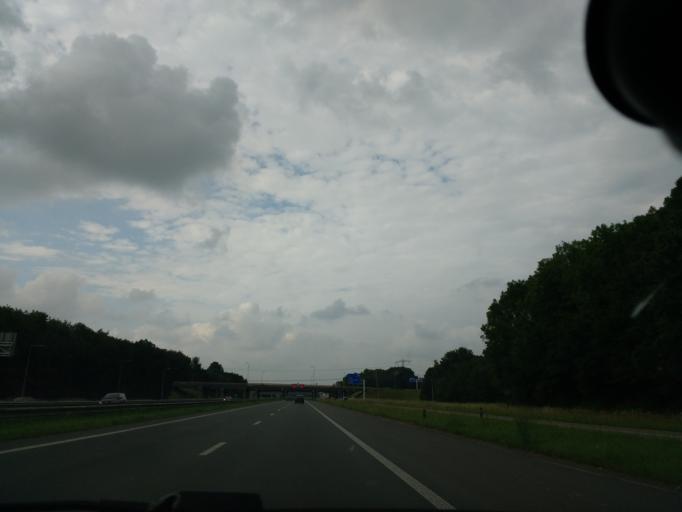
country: NL
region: Gelderland
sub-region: Gemeente Overbetuwe
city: Elst
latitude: 51.8941
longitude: 5.8650
